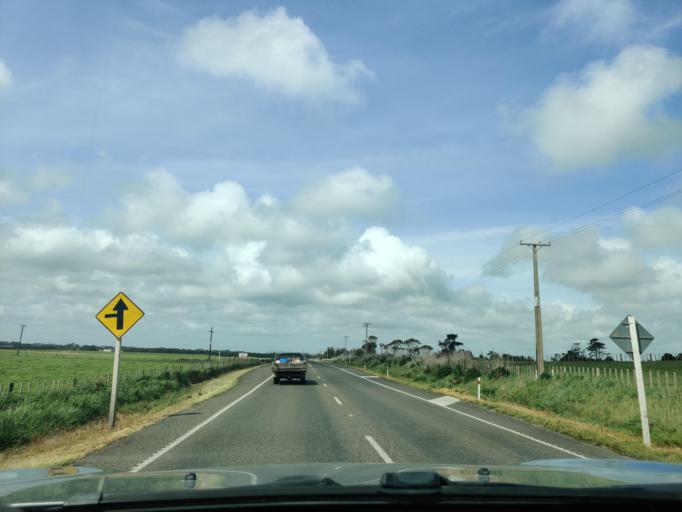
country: NZ
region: Taranaki
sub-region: South Taranaki District
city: Patea
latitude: -39.7676
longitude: 174.6041
